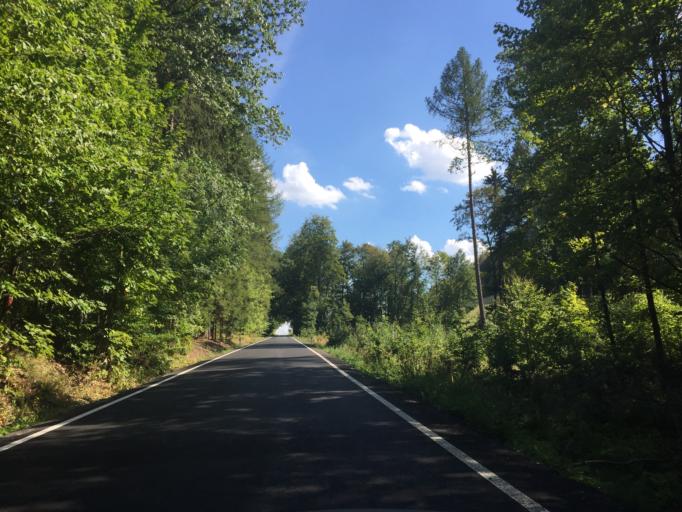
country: CZ
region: Liberecky
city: Mala Skala
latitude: 50.6347
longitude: 15.2116
